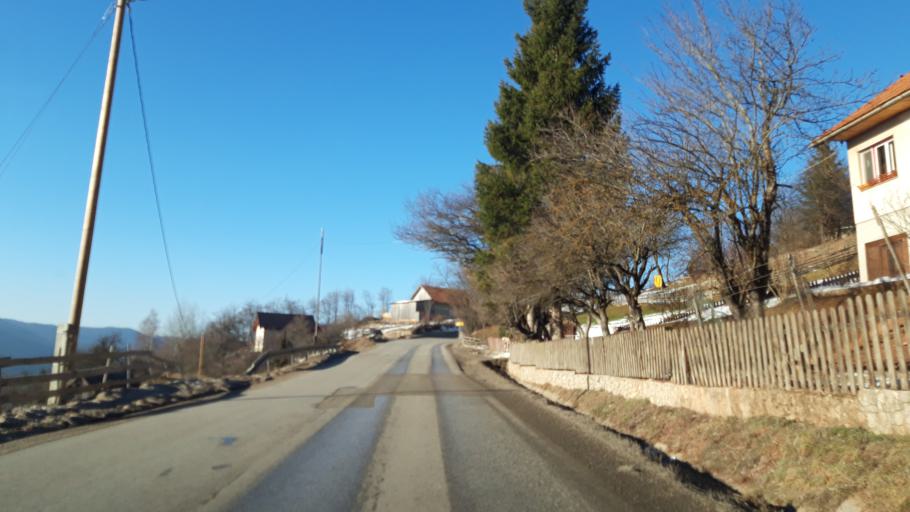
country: BA
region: Republika Srpska
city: Pale
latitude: 43.9034
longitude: 18.6375
